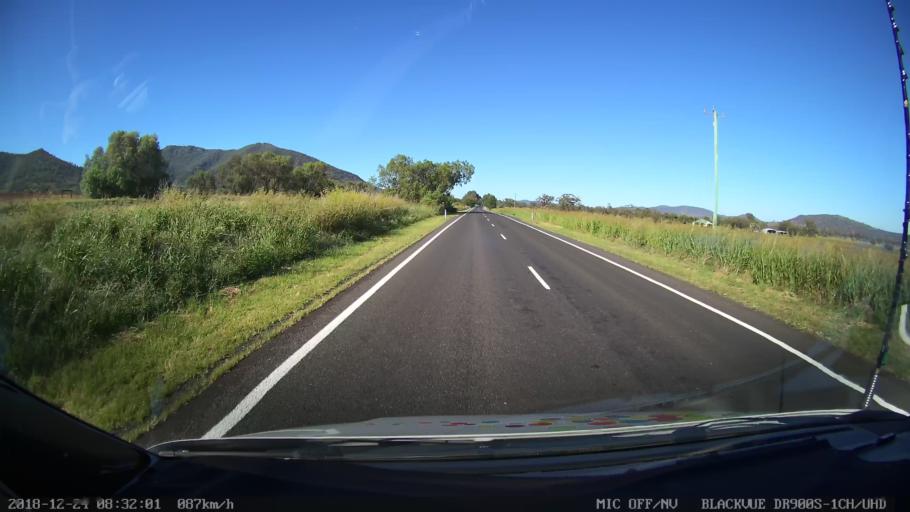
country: AU
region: New South Wales
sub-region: Tamworth Municipality
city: Phillip
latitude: -31.2773
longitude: 150.7037
